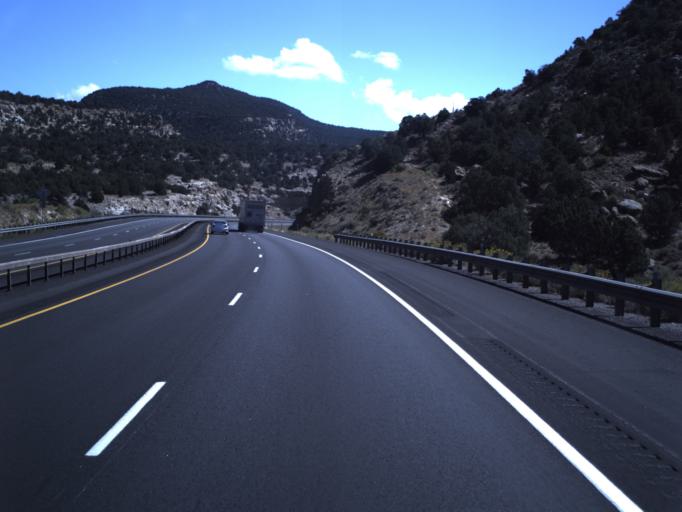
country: US
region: Utah
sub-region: Sevier County
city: Salina
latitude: 38.9095
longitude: -111.7073
